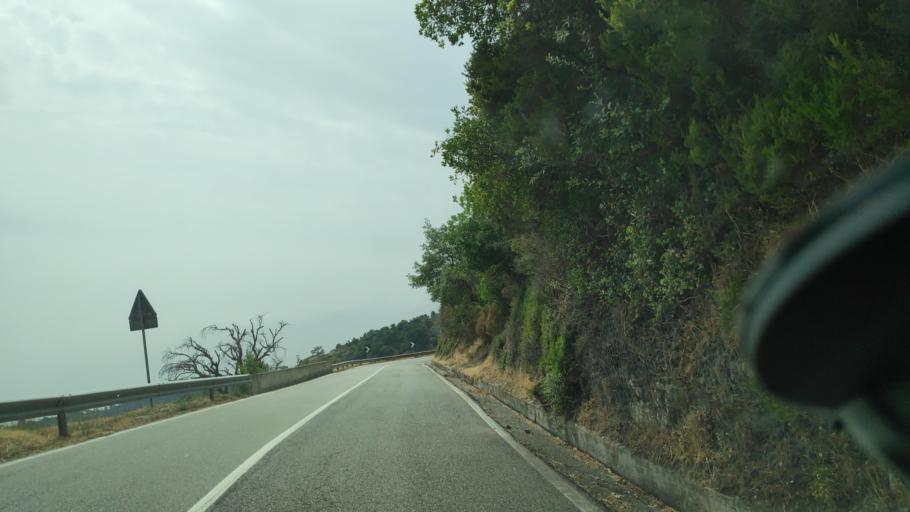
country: IT
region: Calabria
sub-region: Provincia di Catanzaro
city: San Sostene
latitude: 38.6408
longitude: 16.5123
